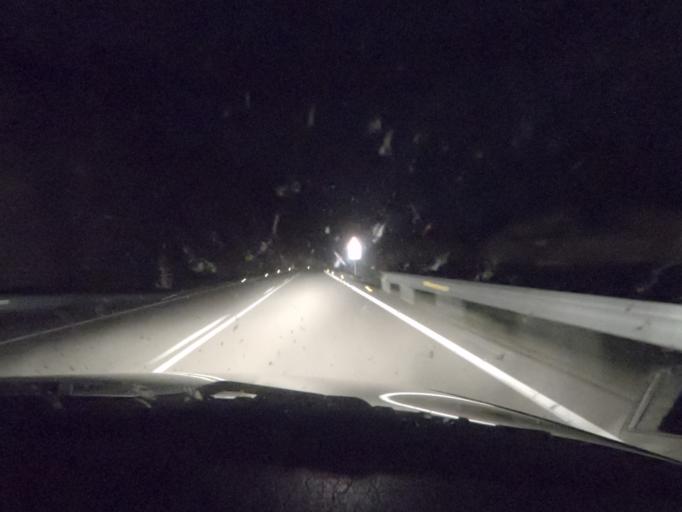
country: ES
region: Extremadura
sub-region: Provincia de Caceres
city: Acebo
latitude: 40.2282
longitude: -6.6801
